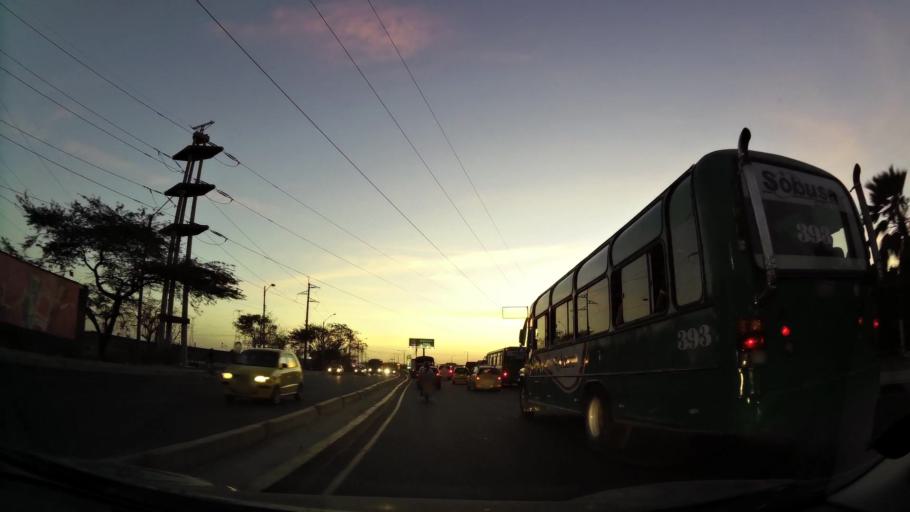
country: CO
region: Atlantico
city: Soledad
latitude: 10.9326
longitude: -74.7820
